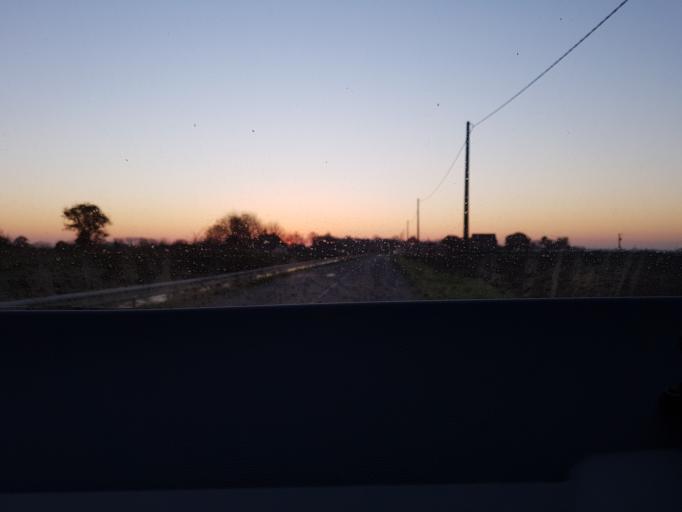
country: FR
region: Nord-Pas-de-Calais
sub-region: Departement du Nord
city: Spycker
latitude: 50.9605
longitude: 2.3304
